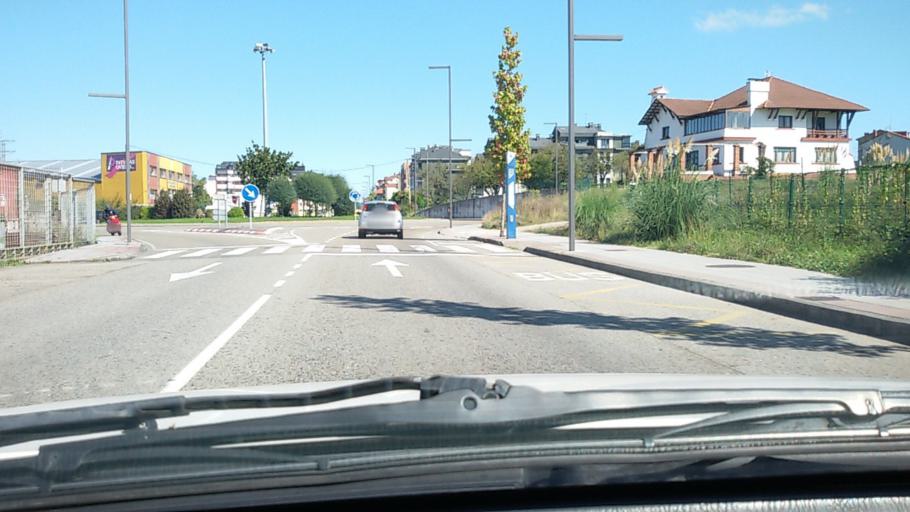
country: ES
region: Asturias
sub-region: Province of Asturias
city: Lugones
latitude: 43.3970
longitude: -5.8141
